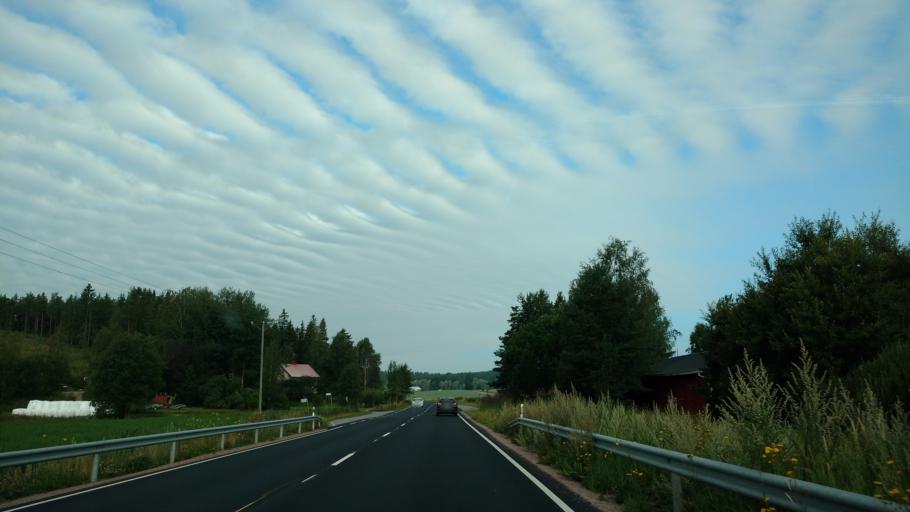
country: FI
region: Varsinais-Suomi
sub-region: Aboland-Turunmaa
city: Kimito
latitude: 60.1697
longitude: 22.7720
